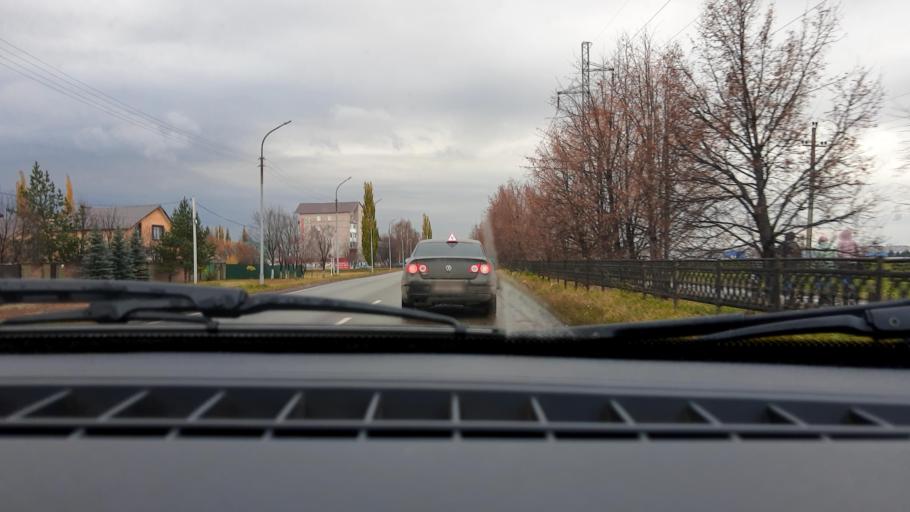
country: RU
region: Bashkortostan
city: Ufa
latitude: 54.8334
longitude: 55.9955
